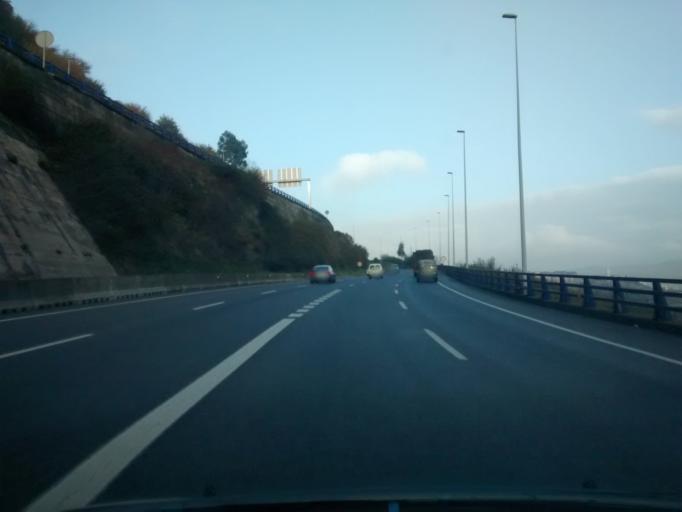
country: ES
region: Basque Country
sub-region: Bizkaia
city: Santutxu
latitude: 43.2357
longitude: -2.9187
